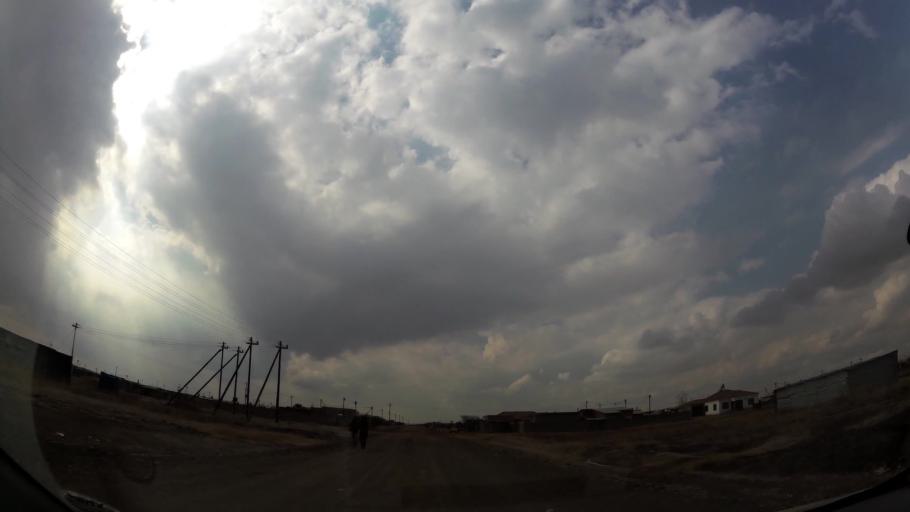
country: ZA
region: Orange Free State
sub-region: Fezile Dabi District Municipality
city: Sasolburg
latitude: -26.8551
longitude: 27.8985
